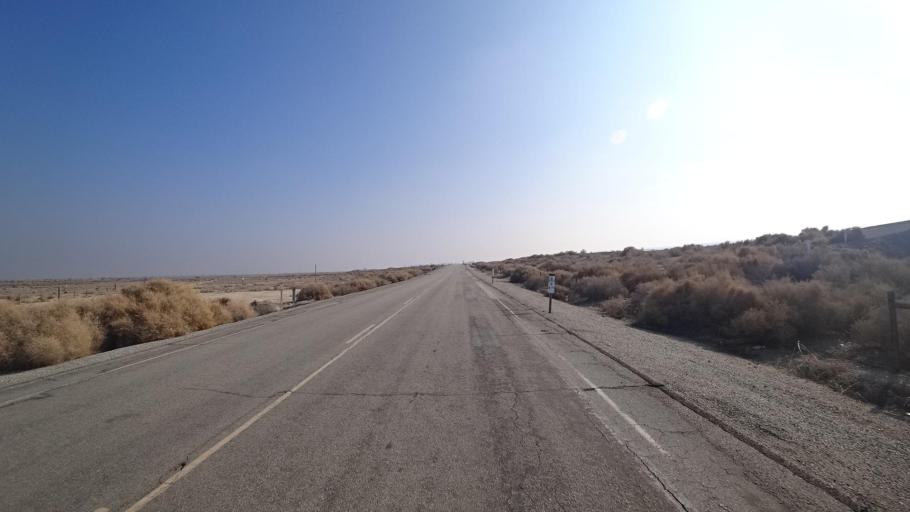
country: US
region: California
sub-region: Kern County
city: Buttonwillow
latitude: 35.3075
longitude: -119.3724
